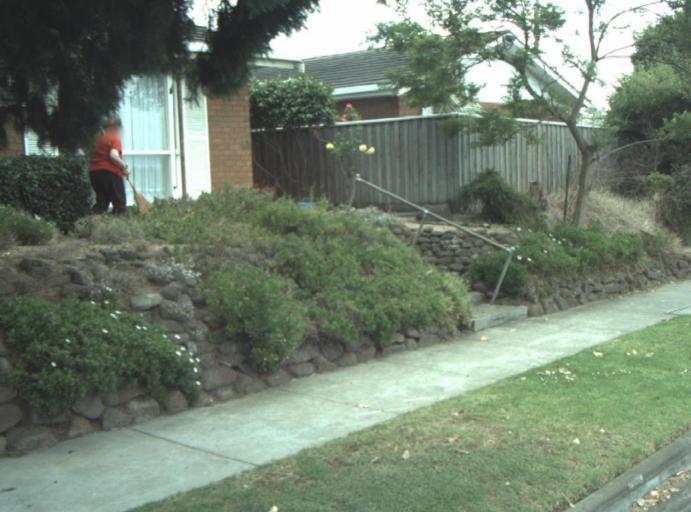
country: AU
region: Victoria
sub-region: Greater Geelong
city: Wandana Heights
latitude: -38.1729
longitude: 144.3183
